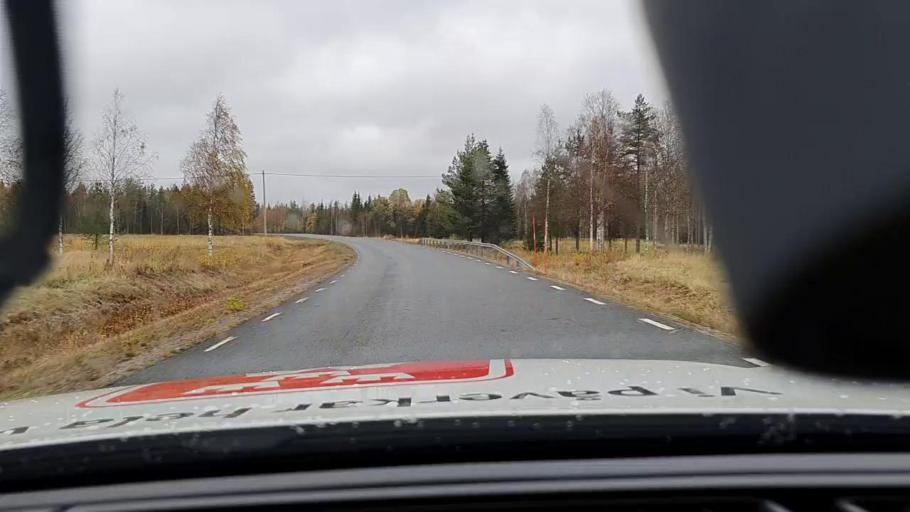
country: SE
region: Norrbotten
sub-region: Haparanda Kommun
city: Haparanda
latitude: 65.9329
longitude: 23.8150
